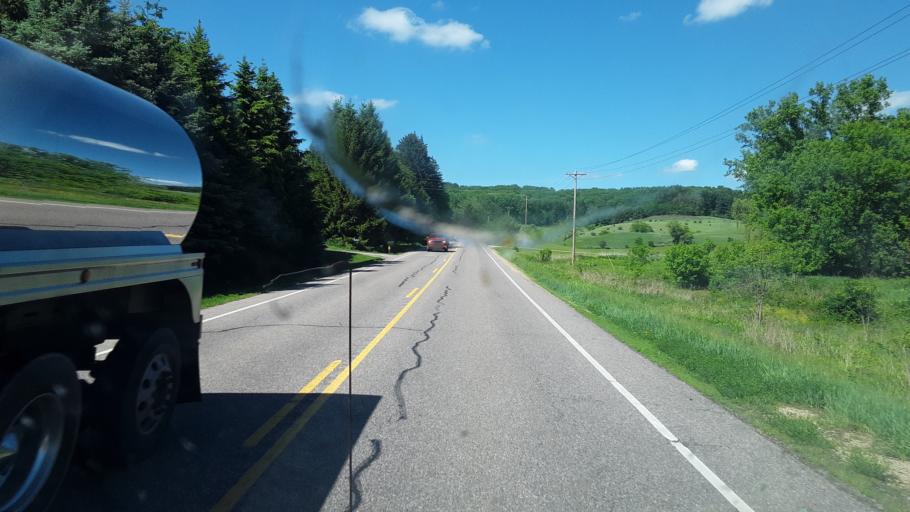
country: US
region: Wisconsin
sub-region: Sauk County
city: Reedsburg
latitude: 43.6101
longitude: -90.1215
